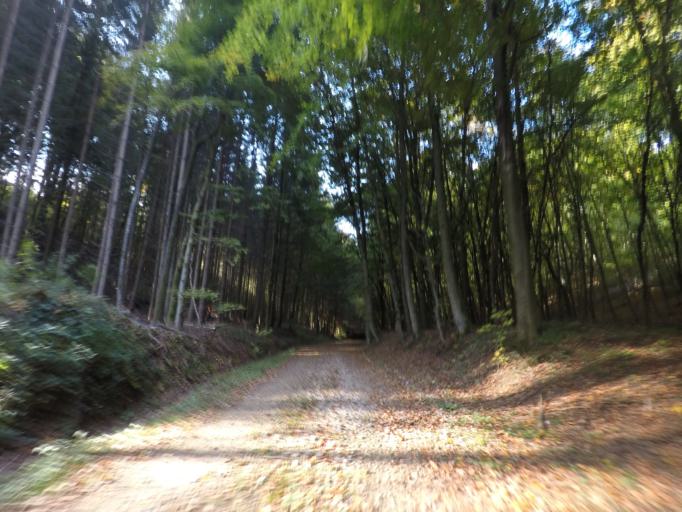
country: LU
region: Luxembourg
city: Itzig
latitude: 49.5990
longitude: 6.1659
